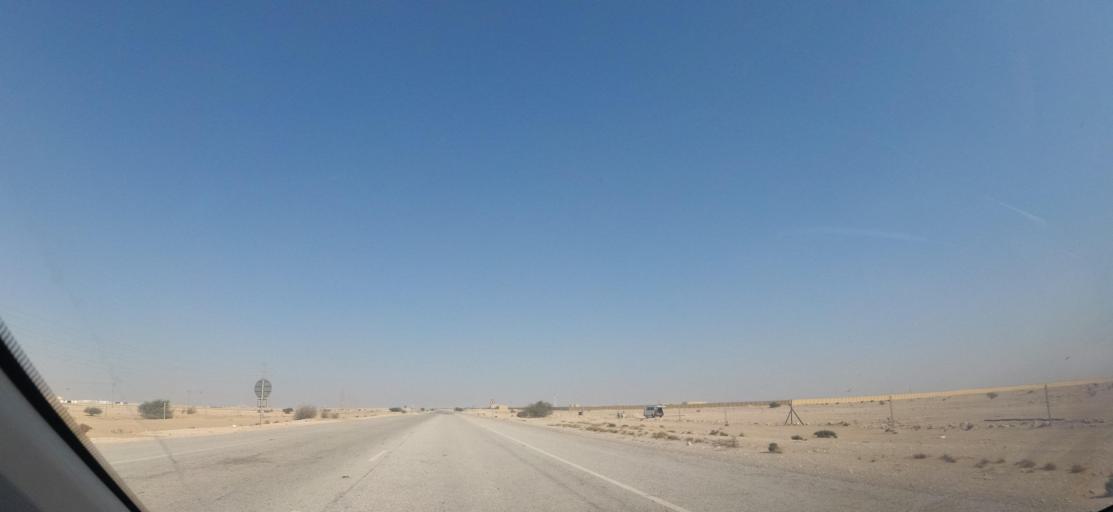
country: QA
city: Al Jumayliyah
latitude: 25.4820
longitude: 50.9636
